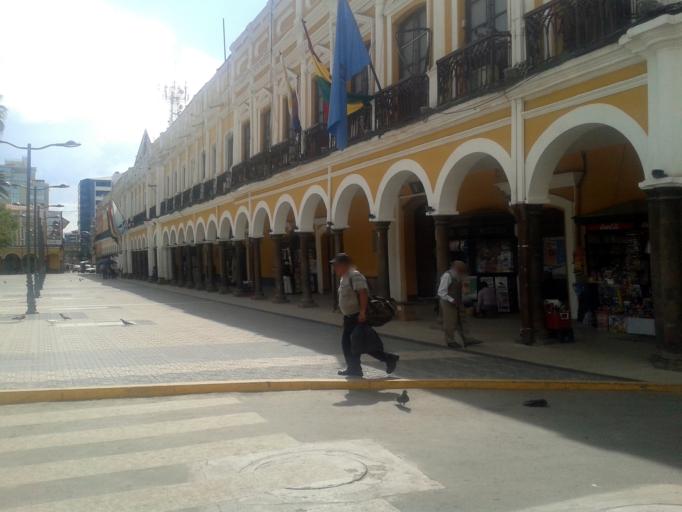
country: BO
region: Cochabamba
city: Cochabamba
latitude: -17.3932
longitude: -66.1566
